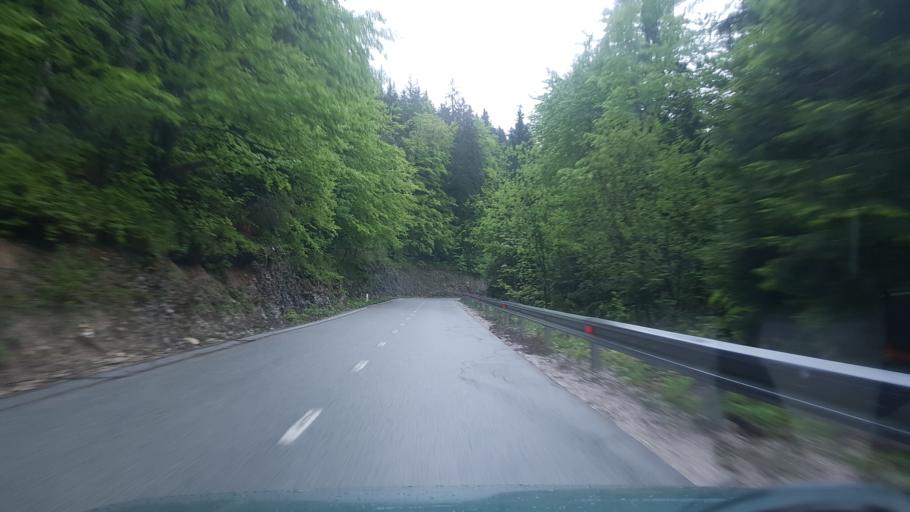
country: SI
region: Bohinj
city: Bohinjska Bistrica
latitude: 46.2610
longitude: 14.0080
